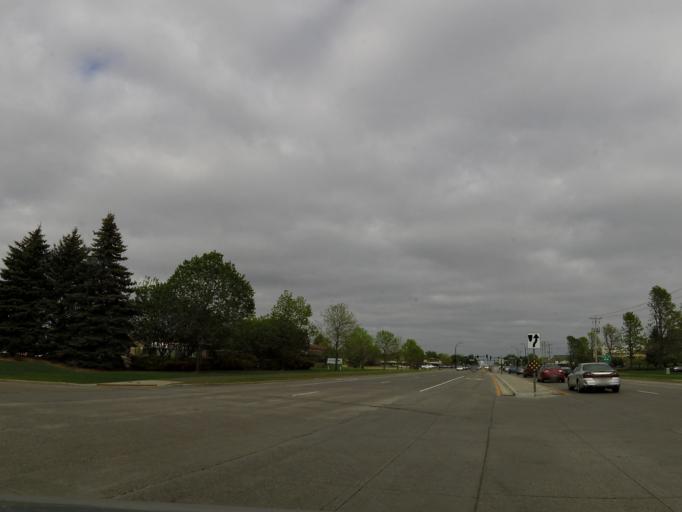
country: US
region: Minnesota
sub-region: Washington County
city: Woodbury
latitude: 44.9199
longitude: -92.9371
